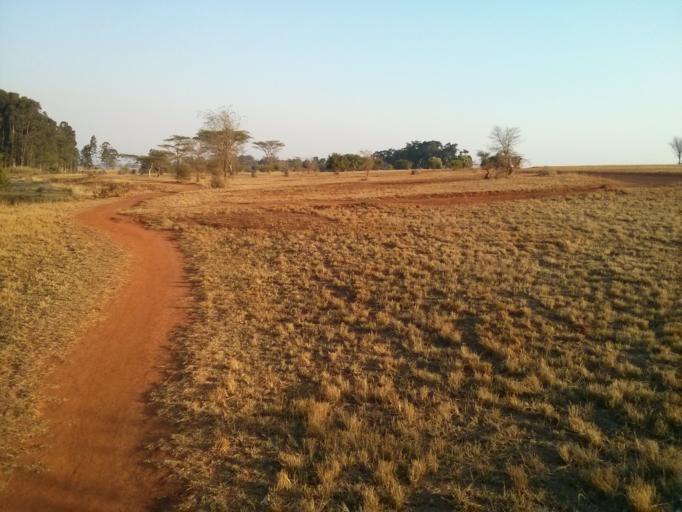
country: SZ
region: Hhohho
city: Lobamba
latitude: -26.4842
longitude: 31.1847
